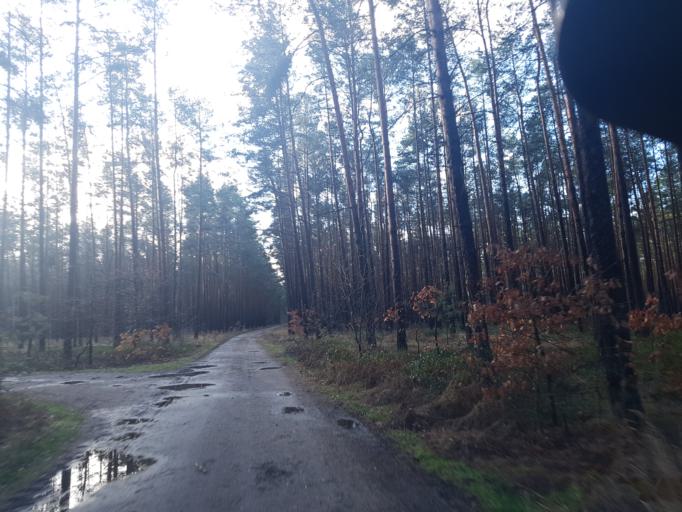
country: DE
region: Brandenburg
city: Ruckersdorf
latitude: 51.5867
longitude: 13.6016
